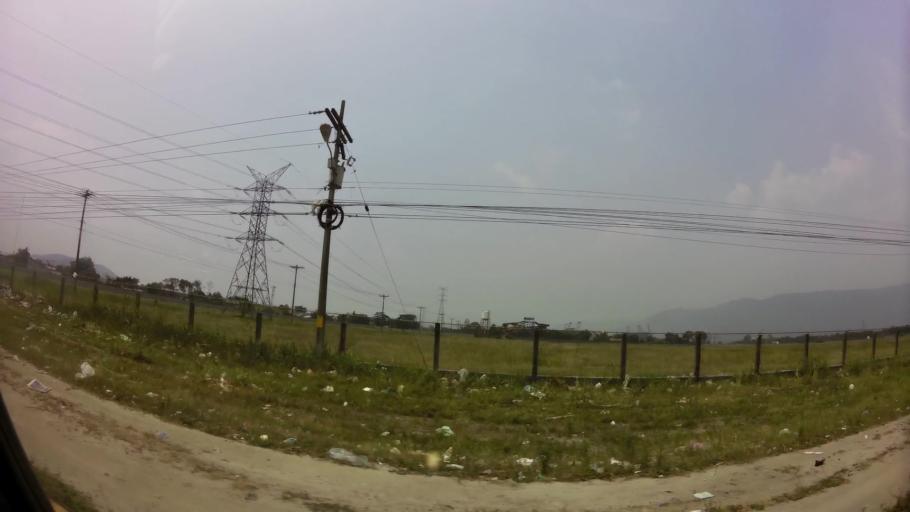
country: HN
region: Cortes
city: San Pedro Sula
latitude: 15.4786
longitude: -88.0031
